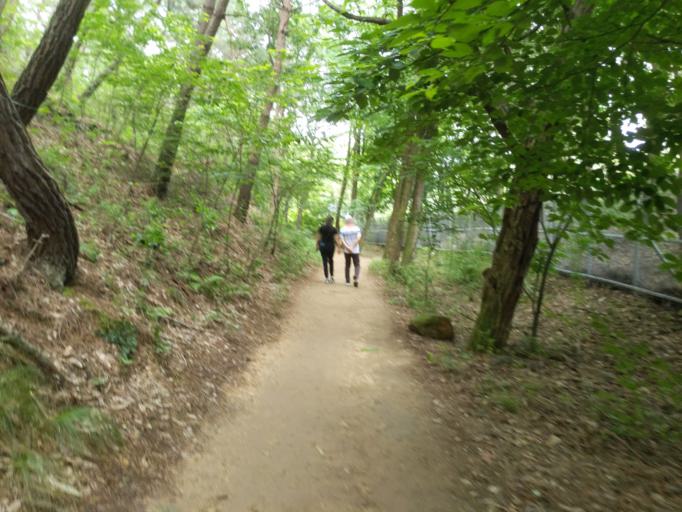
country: KR
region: Daegu
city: Hwawon
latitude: 35.7949
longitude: 128.5262
